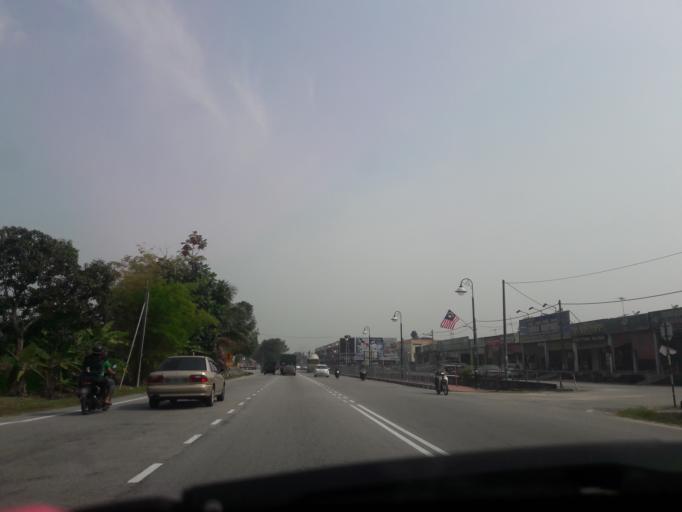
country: MY
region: Kedah
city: Kulim
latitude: 5.3748
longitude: 100.5401
